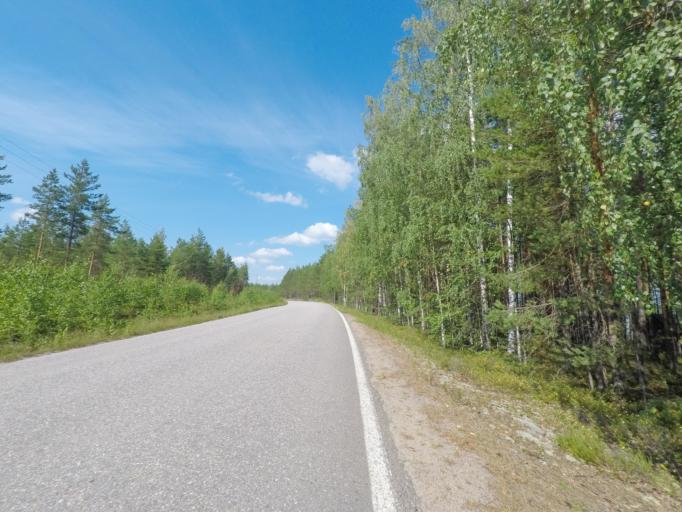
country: FI
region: Southern Savonia
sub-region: Mikkeli
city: Puumala
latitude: 61.4799
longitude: 28.1722
